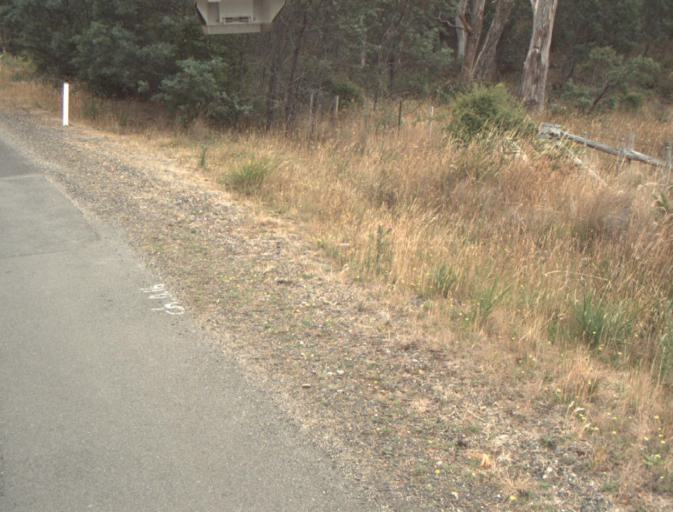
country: AU
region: Tasmania
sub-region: Northern Midlands
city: Evandale
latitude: -41.5064
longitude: 147.3808
